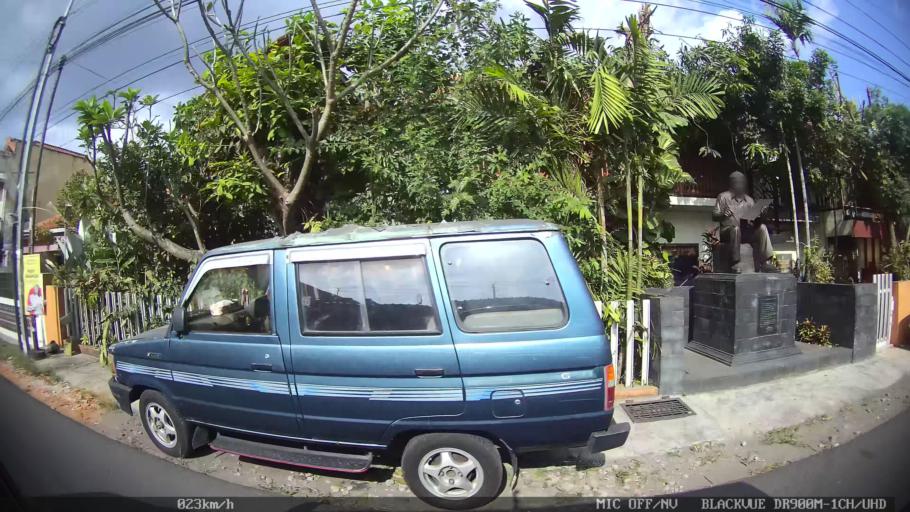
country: ID
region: Daerah Istimewa Yogyakarta
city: Gamping Lor
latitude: -7.7996
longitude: 110.3449
